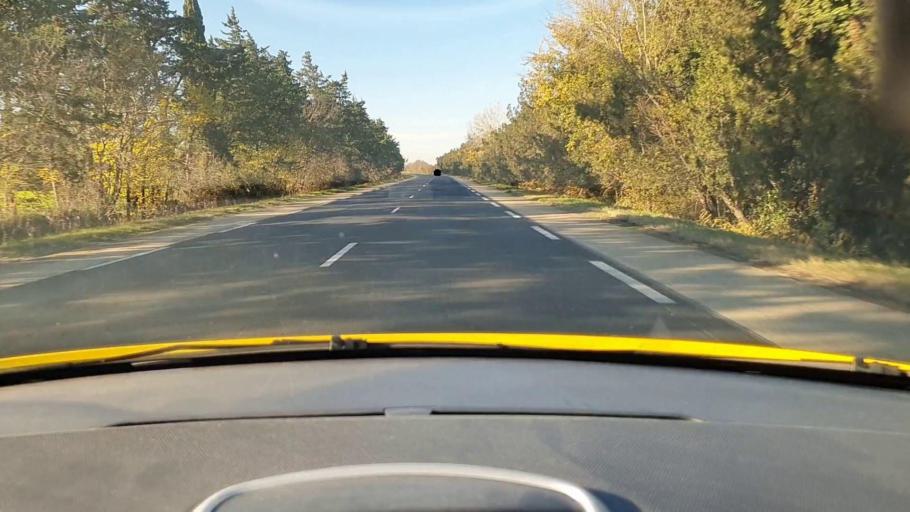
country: FR
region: Languedoc-Roussillon
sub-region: Departement du Gard
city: Fourques
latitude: 43.7021
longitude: 4.5715
